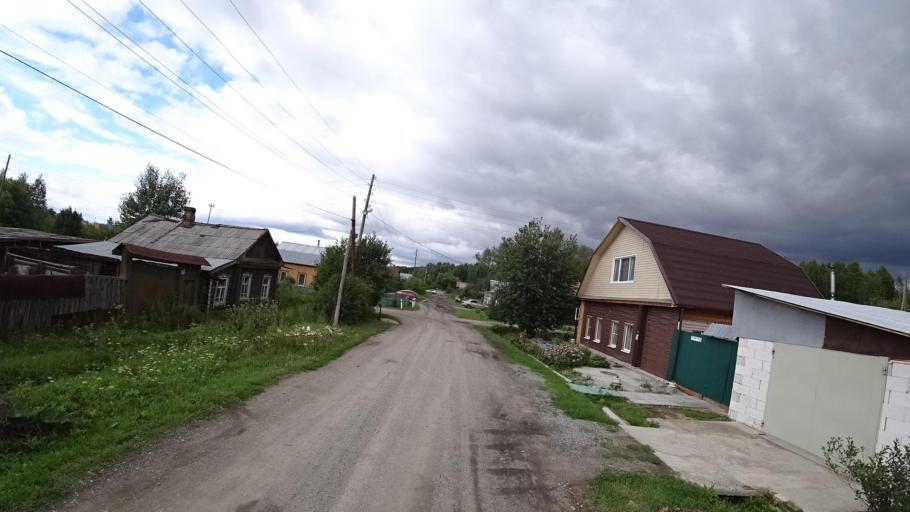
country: RU
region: Sverdlovsk
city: Kamyshlov
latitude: 56.8574
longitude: 62.7185
